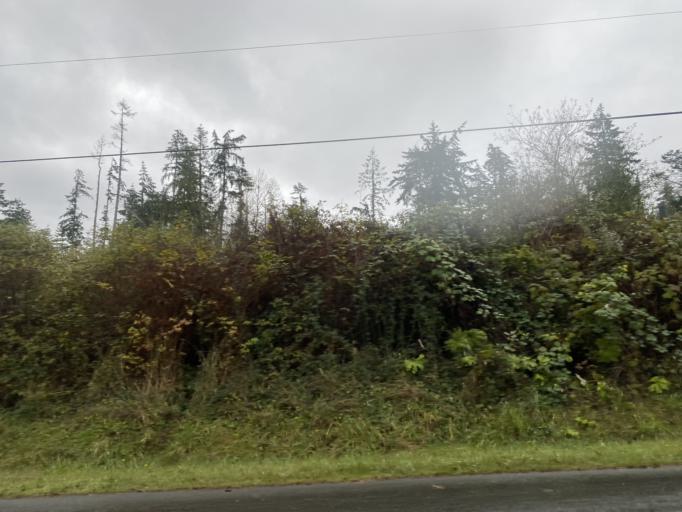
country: US
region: Washington
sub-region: Island County
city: Freeland
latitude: 48.0877
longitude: -122.4852
